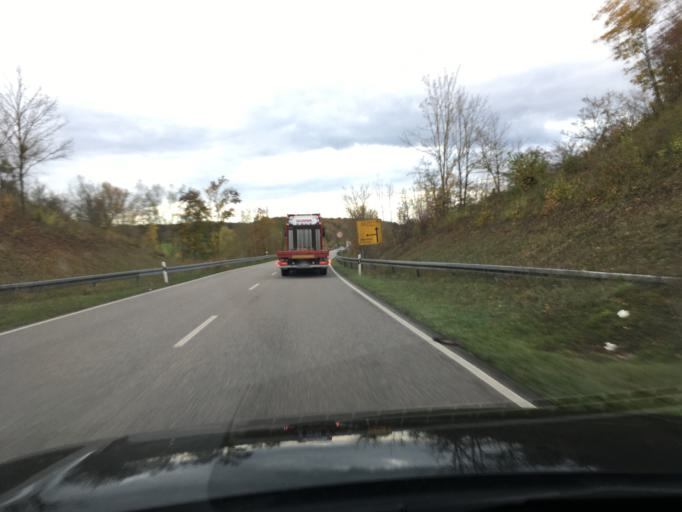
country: DE
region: Baden-Wuerttemberg
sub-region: Karlsruhe Region
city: Zaisenhausen
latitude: 49.0980
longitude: 8.8094
